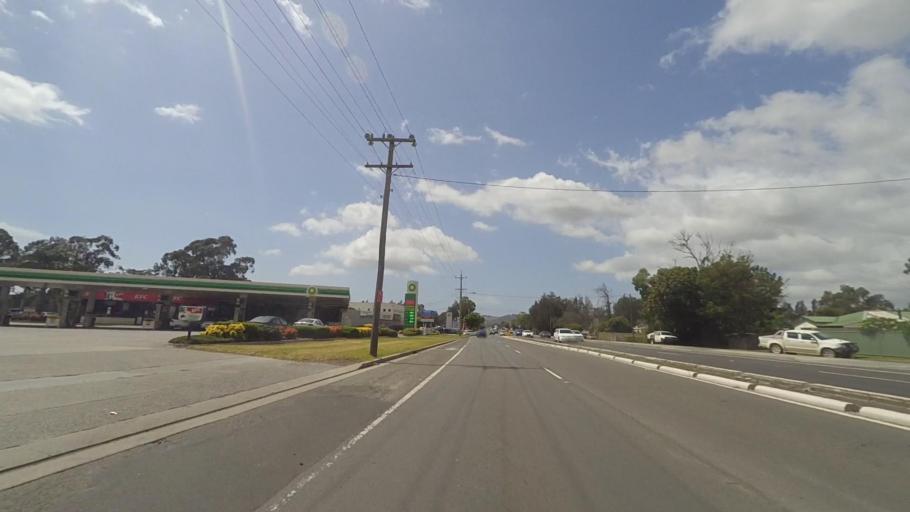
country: AU
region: New South Wales
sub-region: Shellharbour
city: Albion Park Rail
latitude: -34.5544
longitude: 150.7901
